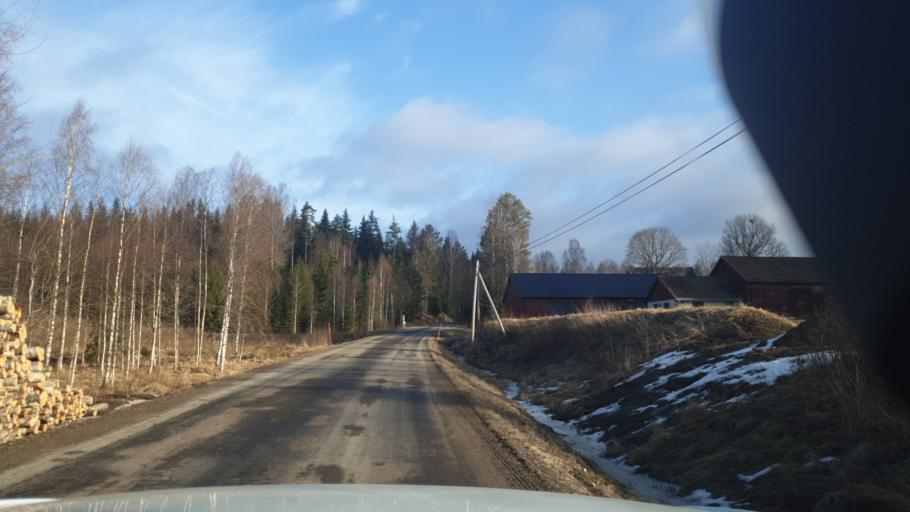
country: SE
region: Vaermland
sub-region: Eda Kommun
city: Amotfors
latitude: 59.8599
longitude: 12.4248
